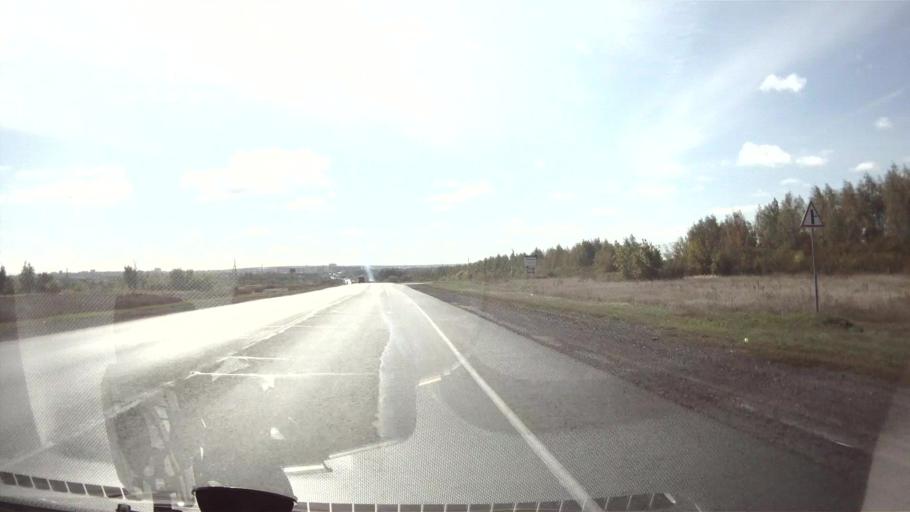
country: RU
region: Ulyanovsk
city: Isheyevka
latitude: 54.3129
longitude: 48.2348
